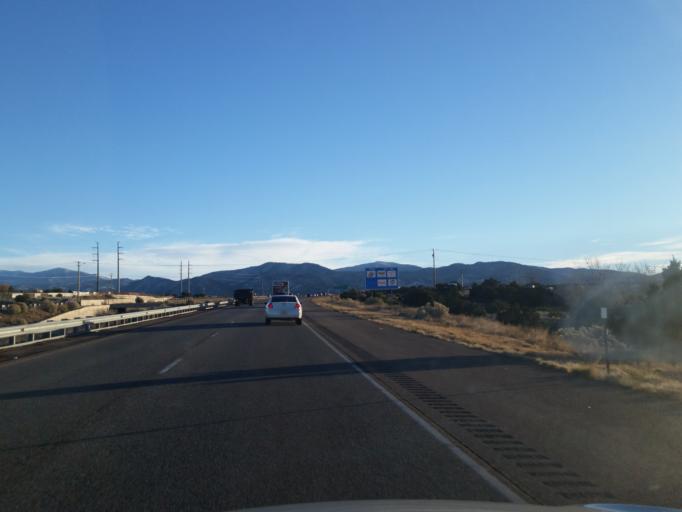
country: US
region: New Mexico
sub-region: Santa Fe County
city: Agua Fria
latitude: 35.6292
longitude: -105.9718
